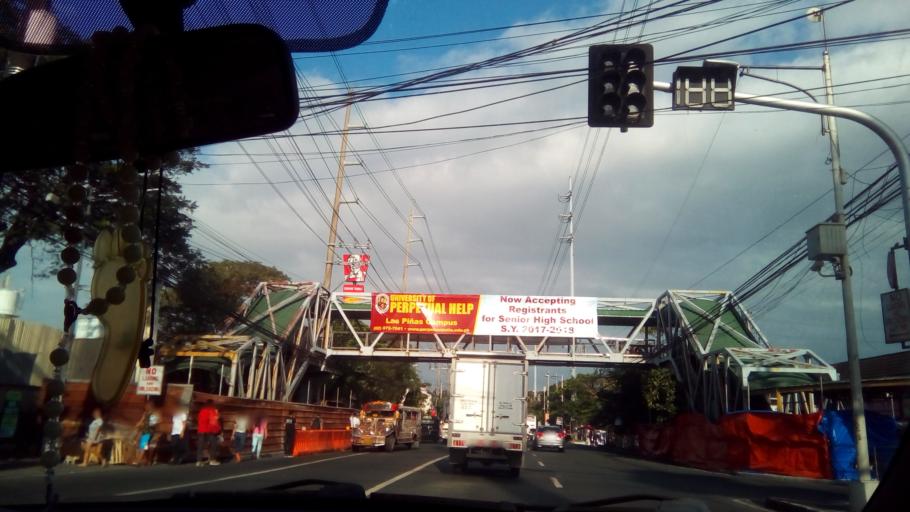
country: PH
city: Sambayanihan People's Village
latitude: 14.4444
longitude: 120.9943
